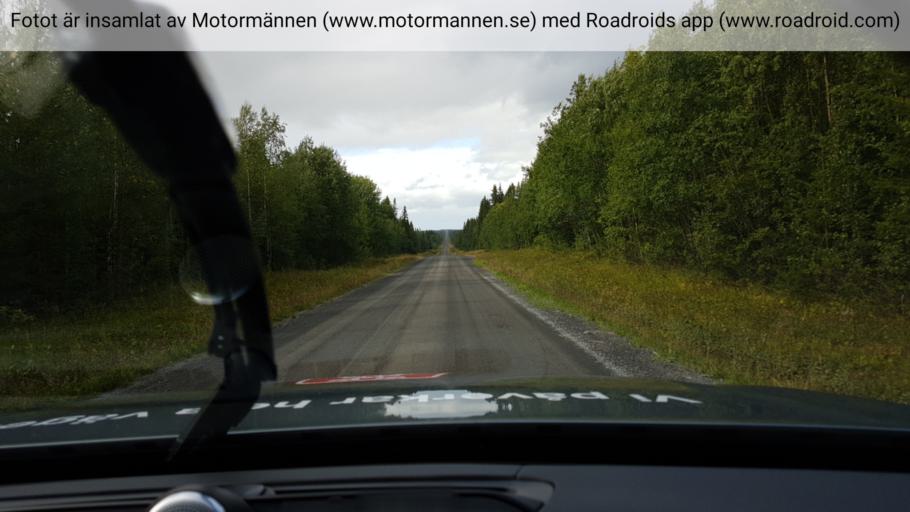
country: SE
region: Jaemtland
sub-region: OEstersunds Kommun
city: Lit
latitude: 63.6483
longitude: 14.9467
